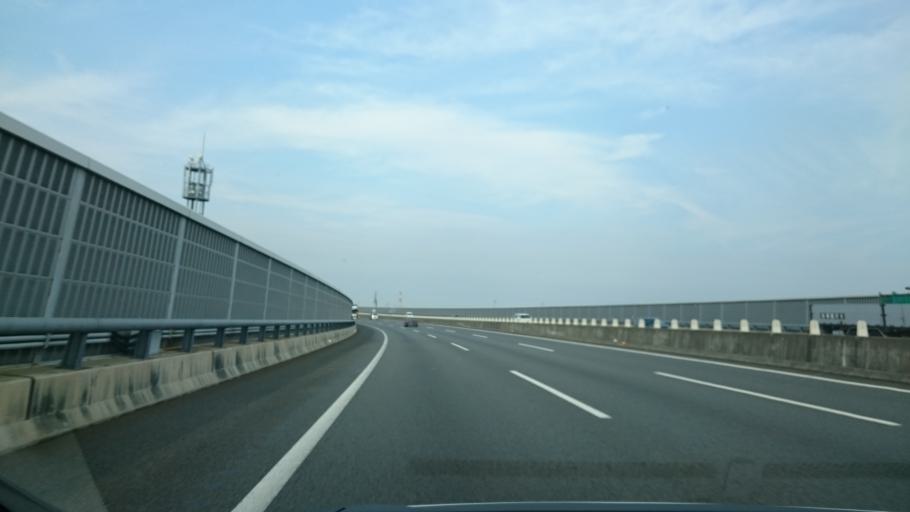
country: JP
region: Mie
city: Yokkaichi
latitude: 35.0265
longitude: 136.6566
